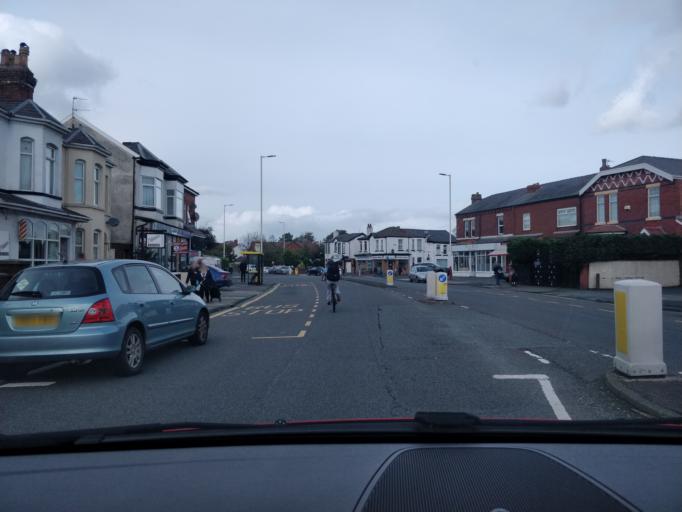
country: GB
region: England
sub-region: Sefton
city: Southport
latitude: 53.6221
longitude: -3.0126
